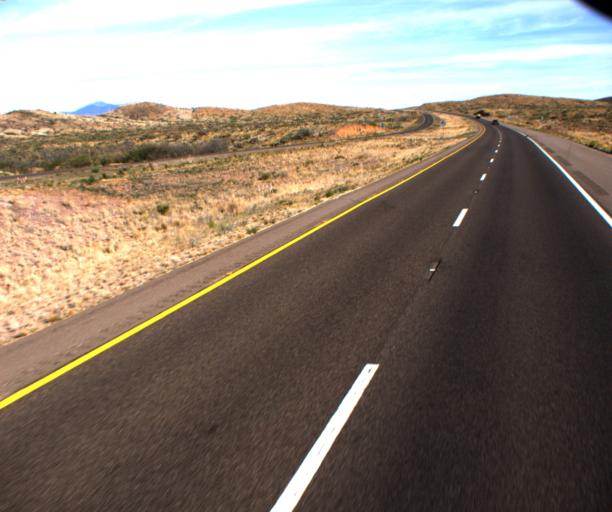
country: US
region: Arizona
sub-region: Cochise County
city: Willcox
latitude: 32.4466
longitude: -109.6633
